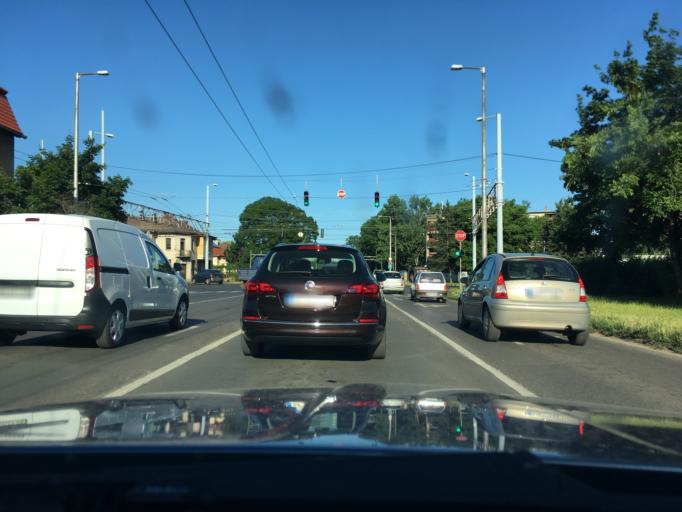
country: HU
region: Hajdu-Bihar
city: Debrecen
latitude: 47.5299
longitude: 21.6384
